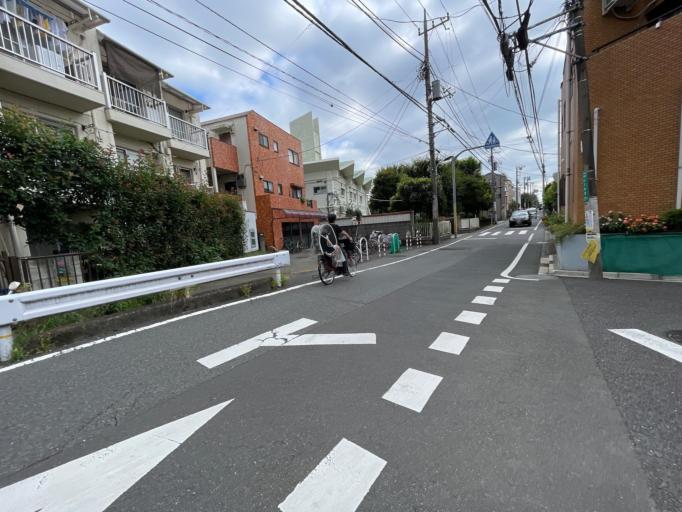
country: JP
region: Tokyo
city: Chofugaoka
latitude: 35.6412
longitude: 139.6121
